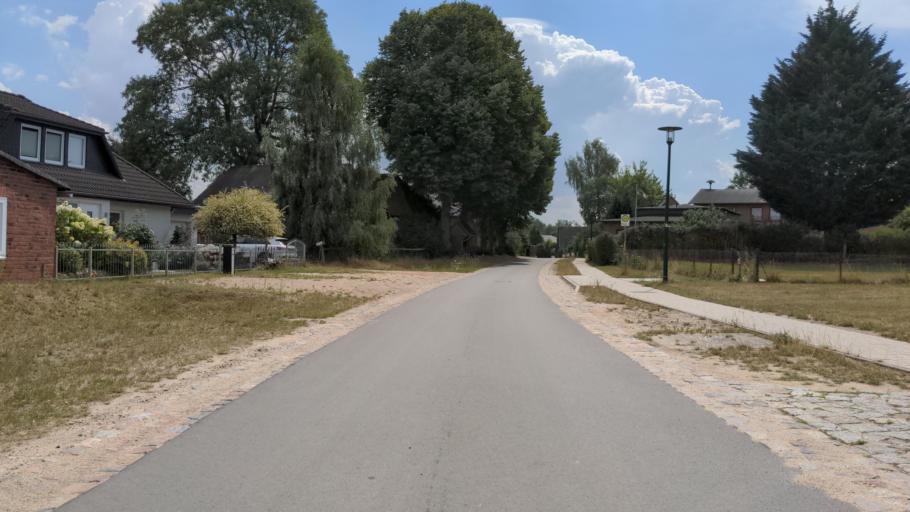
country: DE
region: Mecklenburg-Vorpommern
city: Selmsdorf
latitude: 53.8551
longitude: 10.7995
